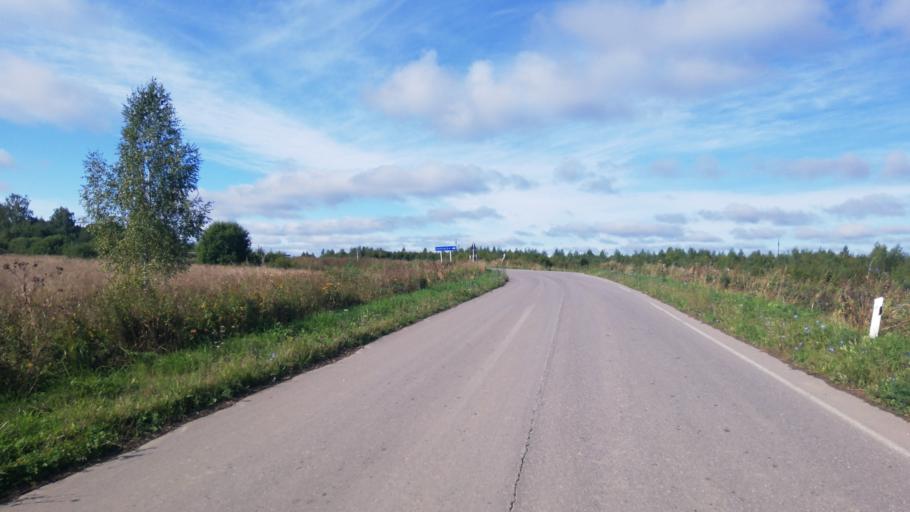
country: RU
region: Ivanovo
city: Novo-Talitsy
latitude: 57.0176
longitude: 40.7599
